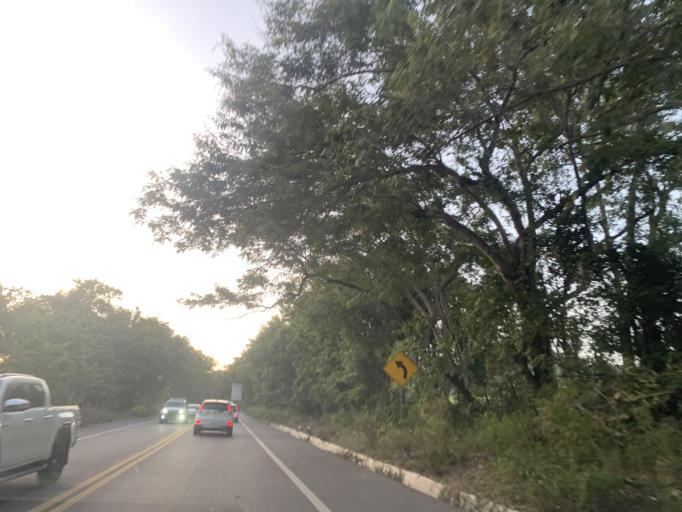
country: DO
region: Puerto Plata
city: Imbert
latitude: 19.7669
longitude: -70.8355
